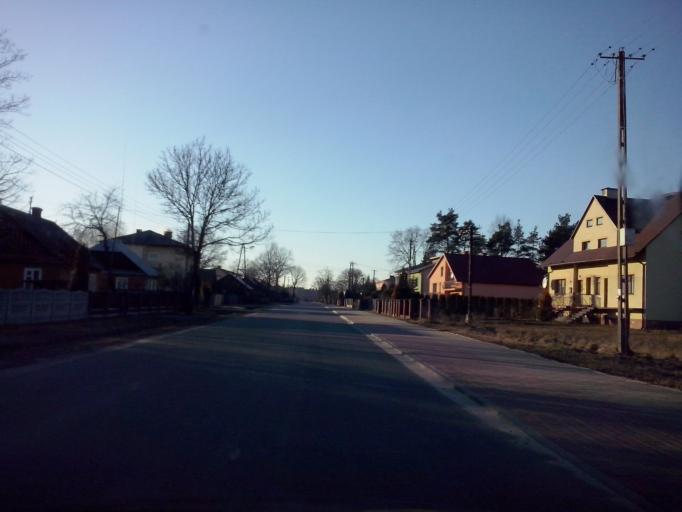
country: PL
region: Subcarpathian Voivodeship
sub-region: Powiat nizanski
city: Harasiuki
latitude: 50.4738
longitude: 22.4809
